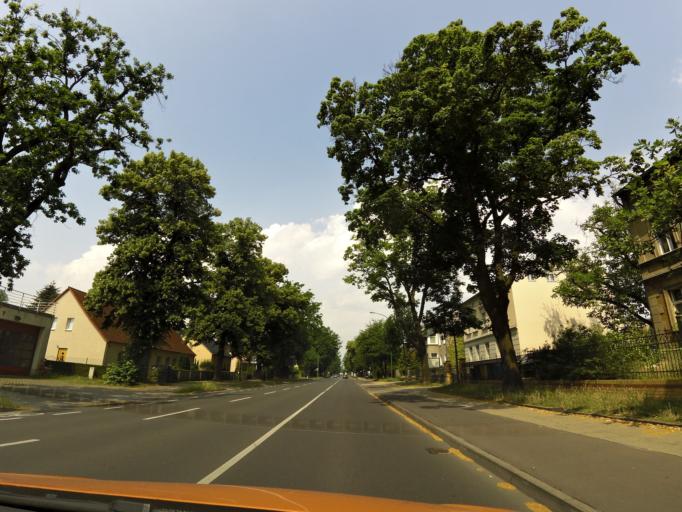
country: DE
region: Brandenburg
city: Potsdam
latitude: 52.4141
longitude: 13.0284
